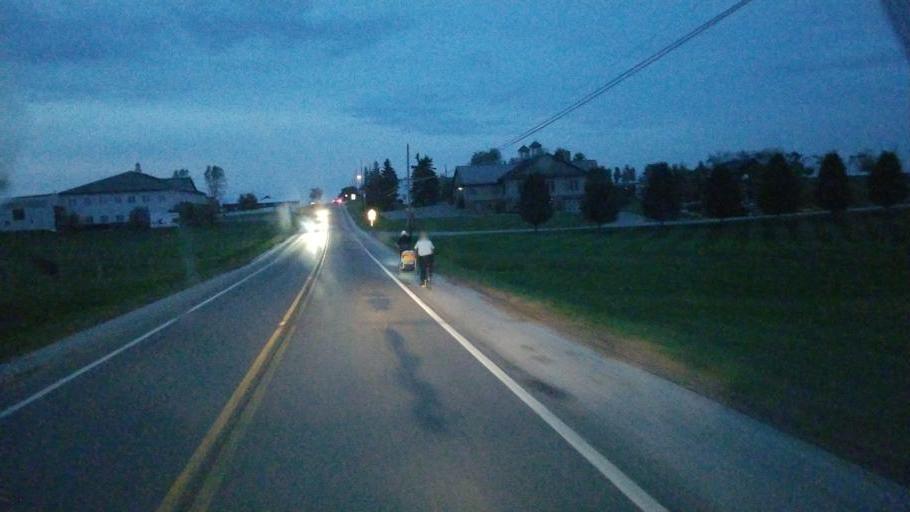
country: US
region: Ohio
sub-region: Wayne County
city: Apple Creek
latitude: 40.6278
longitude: -81.7842
